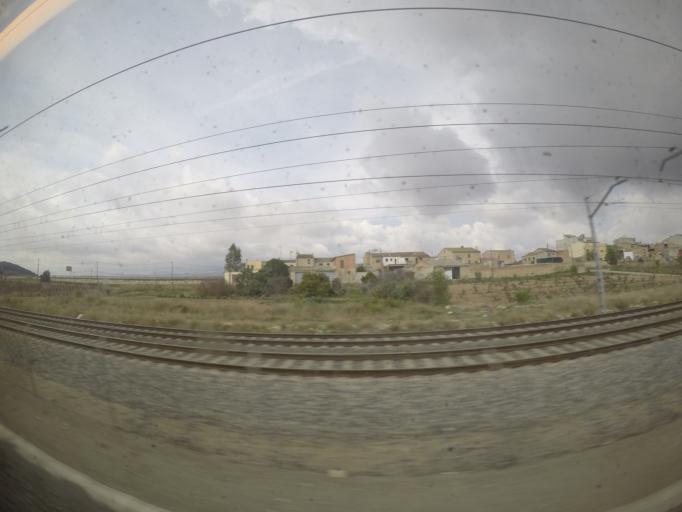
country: ES
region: Catalonia
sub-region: Provincia de Barcelona
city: Castellet
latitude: 41.2846
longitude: 1.6130
